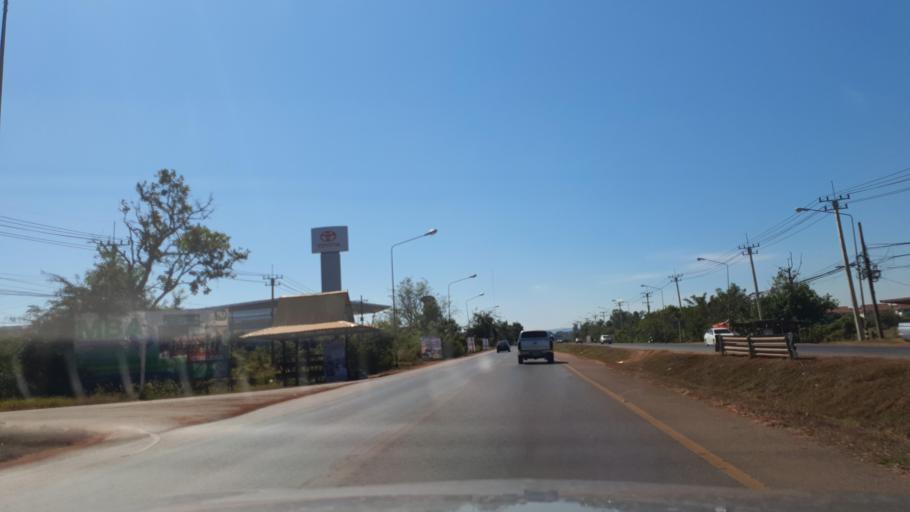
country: TH
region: Sakon Nakhon
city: Sakon Nakhon
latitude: 17.2136
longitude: 104.1033
